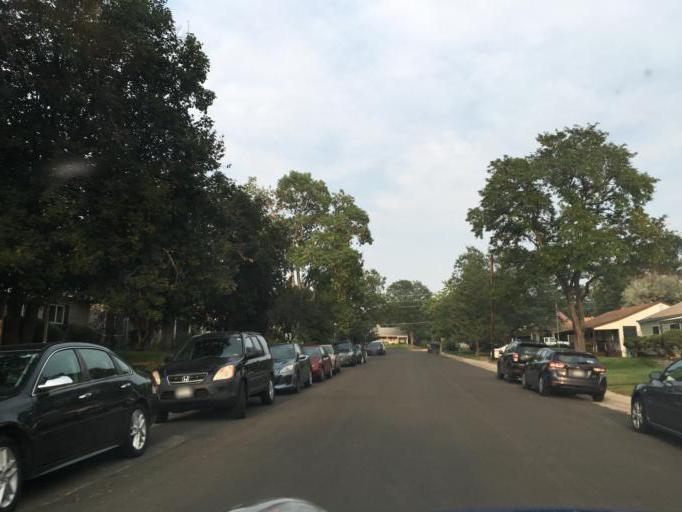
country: US
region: Colorado
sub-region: Arapahoe County
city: Glendale
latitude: 39.6835
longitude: -104.9334
